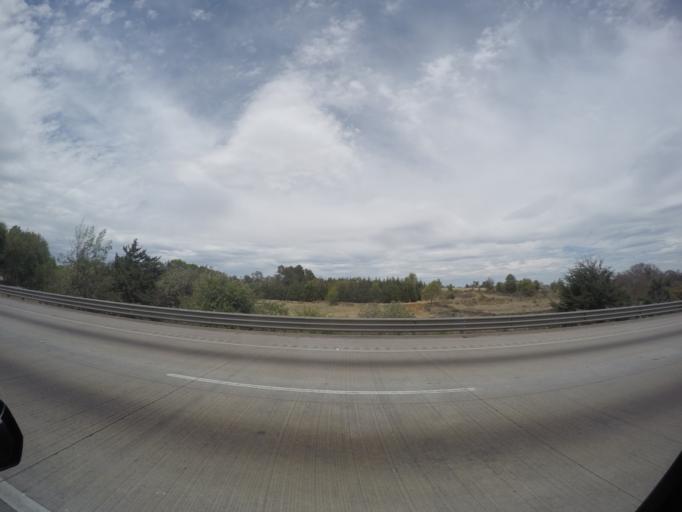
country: MX
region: Mexico
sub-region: Jilotepec
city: La Comunidad
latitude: 20.0395
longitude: -99.5698
